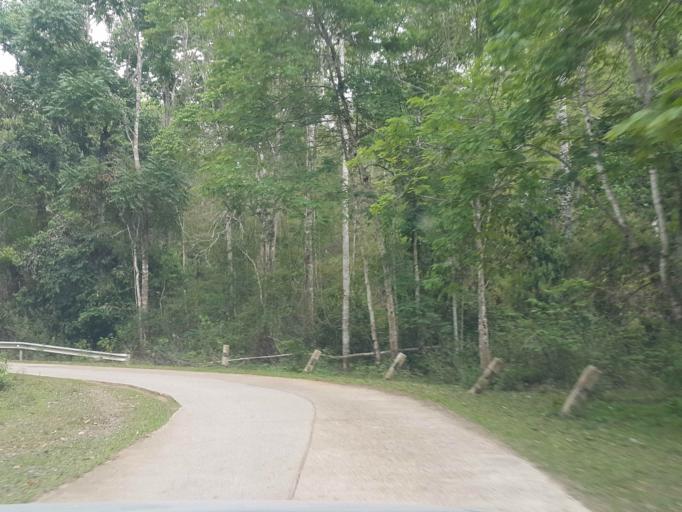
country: TH
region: Chiang Mai
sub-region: Amphoe Chiang Dao
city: Chiang Dao
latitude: 19.3751
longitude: 98.7536
